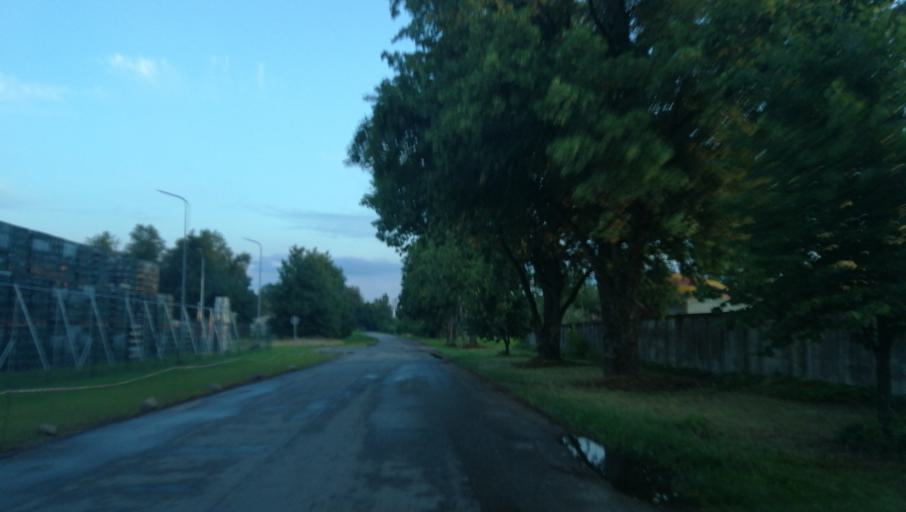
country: LV
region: Cesu Rajons
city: Cesis
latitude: 57.3179
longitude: 25.3027
